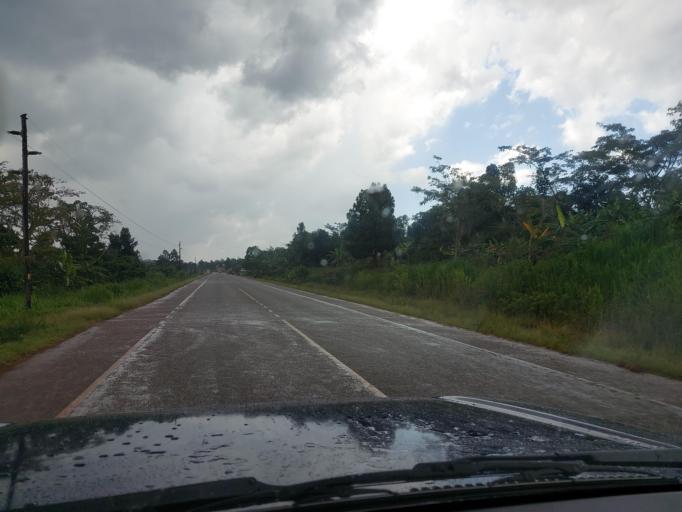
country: UG
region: Central Region
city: Lugazi
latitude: 0.2494
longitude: 32.8863
